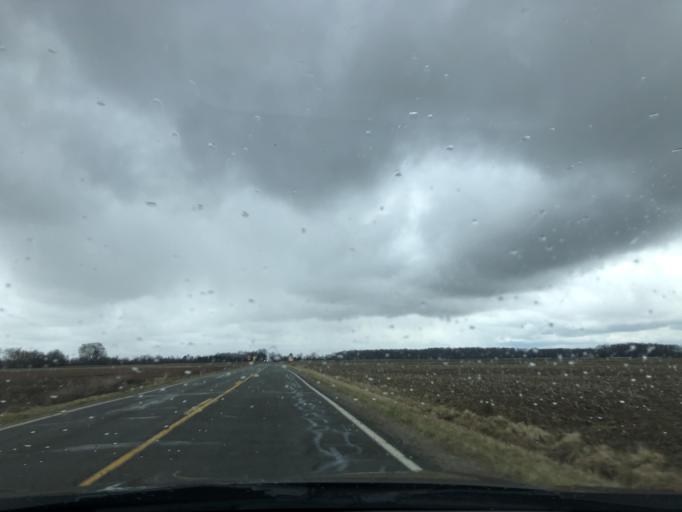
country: US
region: Michigan
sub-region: Clinton County
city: Fowler
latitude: 42.9295
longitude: -84.6584
